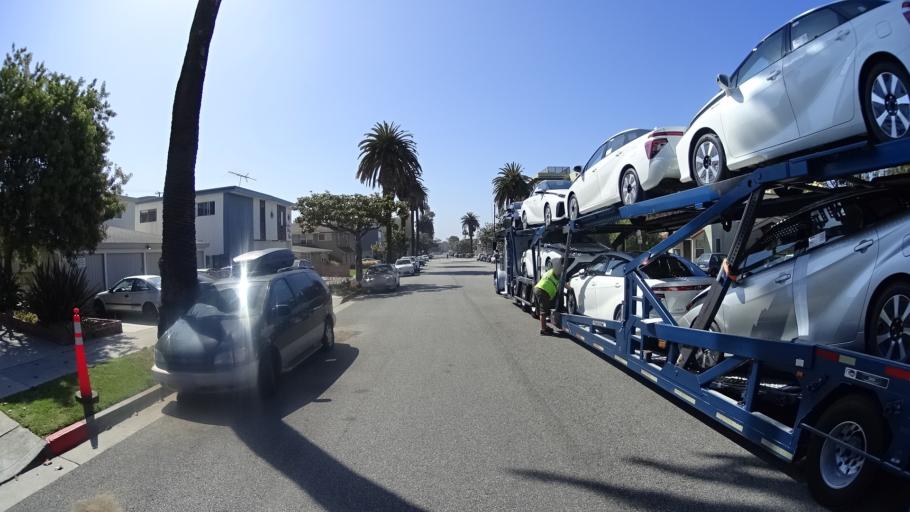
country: US
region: California
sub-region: Los Angeles County
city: Santa Monica
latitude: 34.0197
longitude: -118.4898
